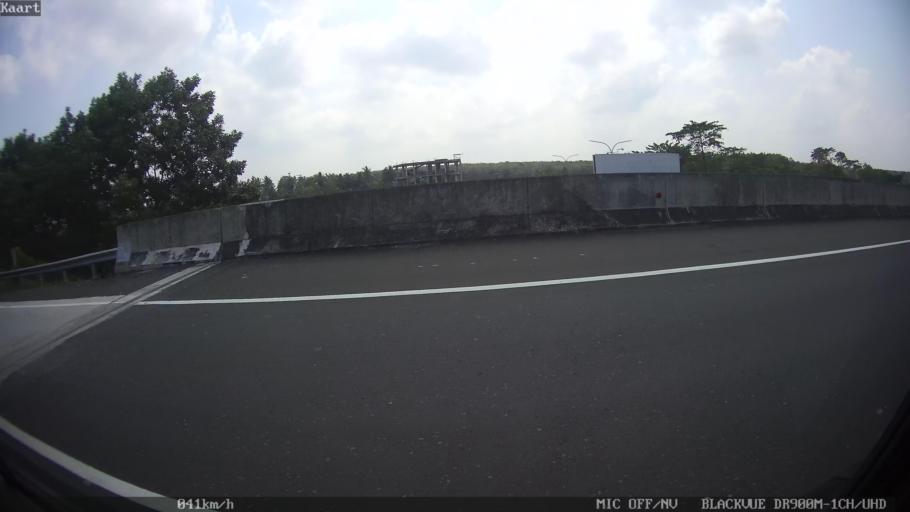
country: ID
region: Lampung
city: Kedaton
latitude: -5.3522
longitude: 105.3227
